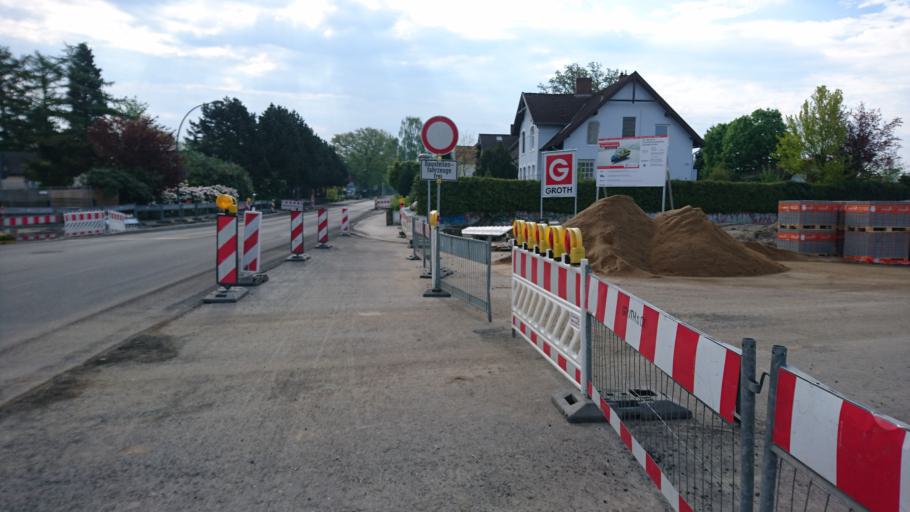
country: DE
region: Schleswig-Holstein
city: Wedel
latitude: 53.5714
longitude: 9.7299
